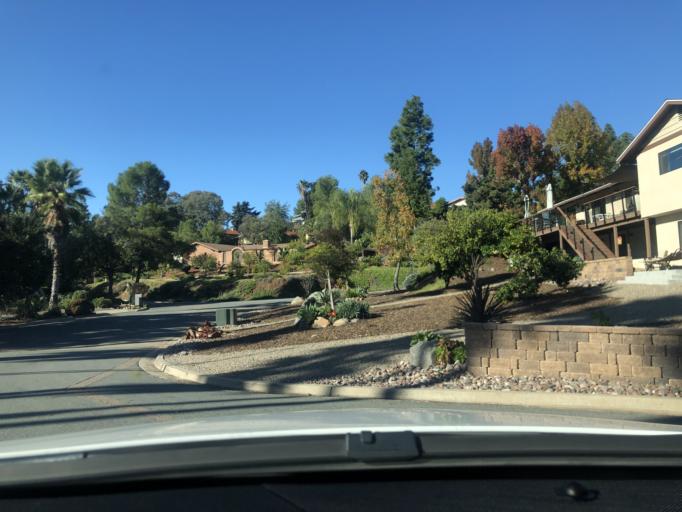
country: US
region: California
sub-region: San Diego County
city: Casa de Oro-Mount Helix
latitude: 32.7675
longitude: -116.9500
